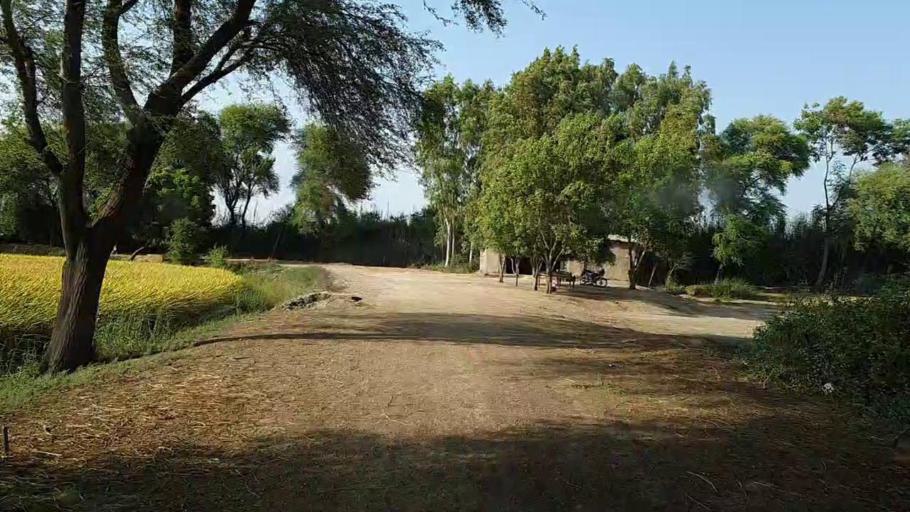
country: PK
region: Sindh
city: Bulri
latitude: 24.7850
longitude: 68.4355
